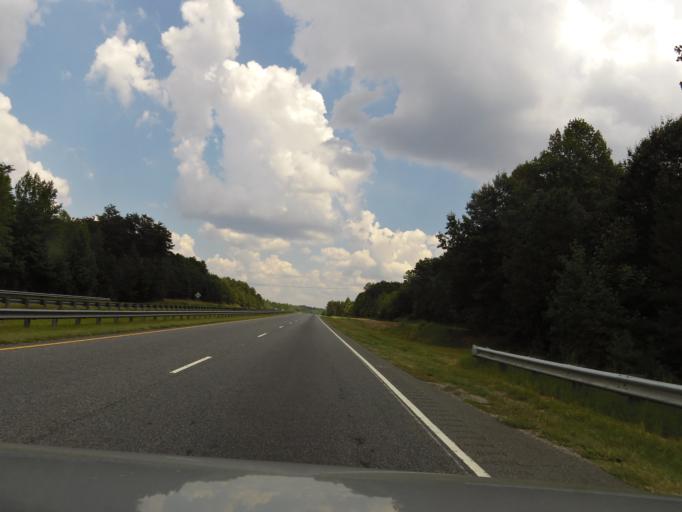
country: US
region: North Carolina
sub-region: Rutherford County
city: Rutherfordton
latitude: 35.2984
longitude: -81.9689
